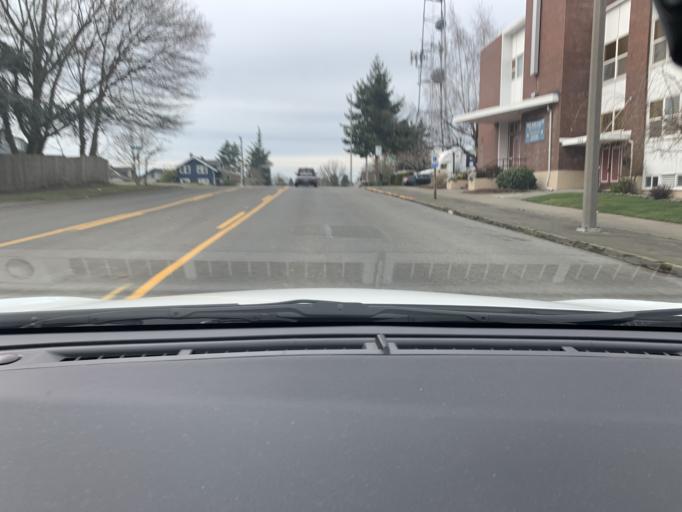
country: US
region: Washington
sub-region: Pierce County
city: Tacoma
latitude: 47.2512
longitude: -122.4597
